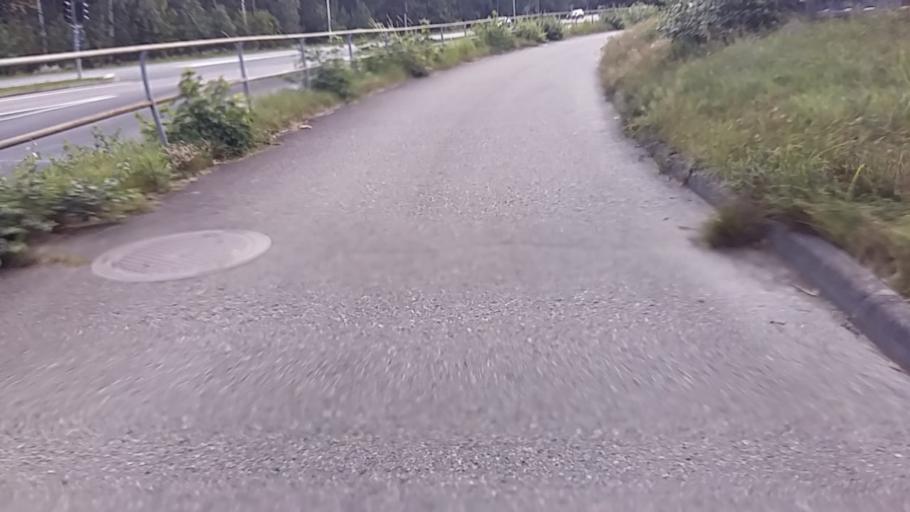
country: SE
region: Joenkoeping
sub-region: Jonkopings Kommun
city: Odensjo
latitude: 57.7463
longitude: 14.1566
